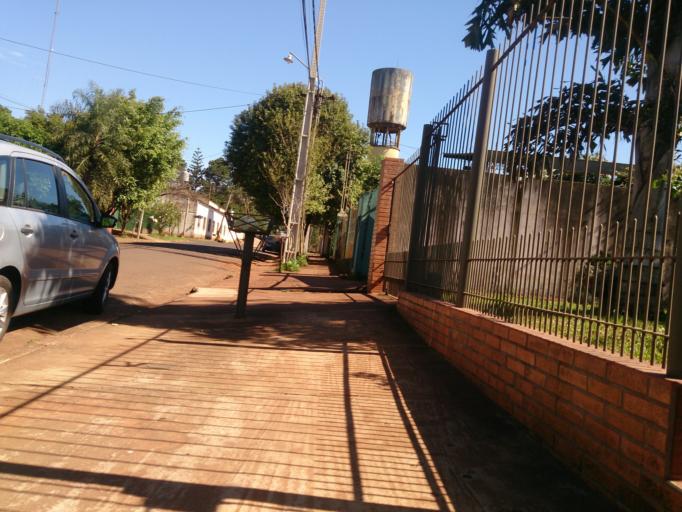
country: AR
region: Misiones
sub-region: Departamento de Obera
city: Obera
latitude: -27.4870
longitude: -55.1093
